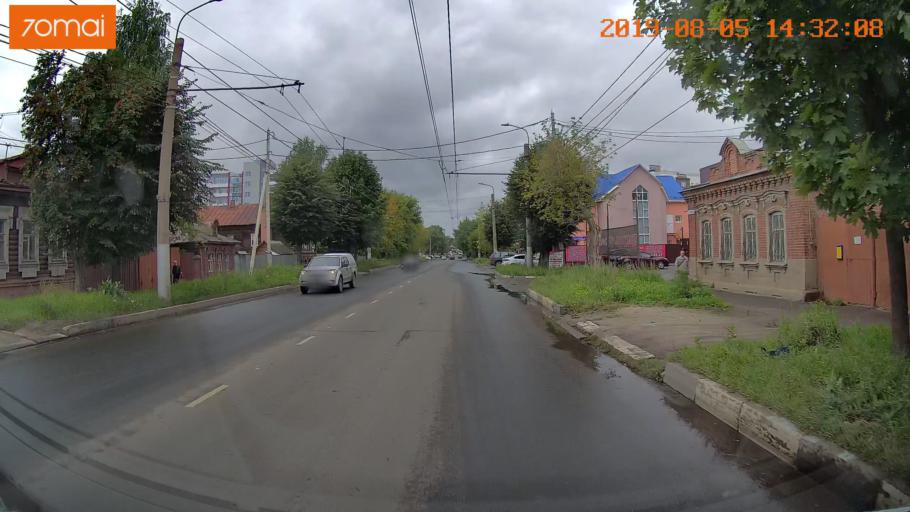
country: RU
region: Ivanovo
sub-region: Gorod Ivanovo
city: Ivanovo
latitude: 56.9899
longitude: 40.9932
